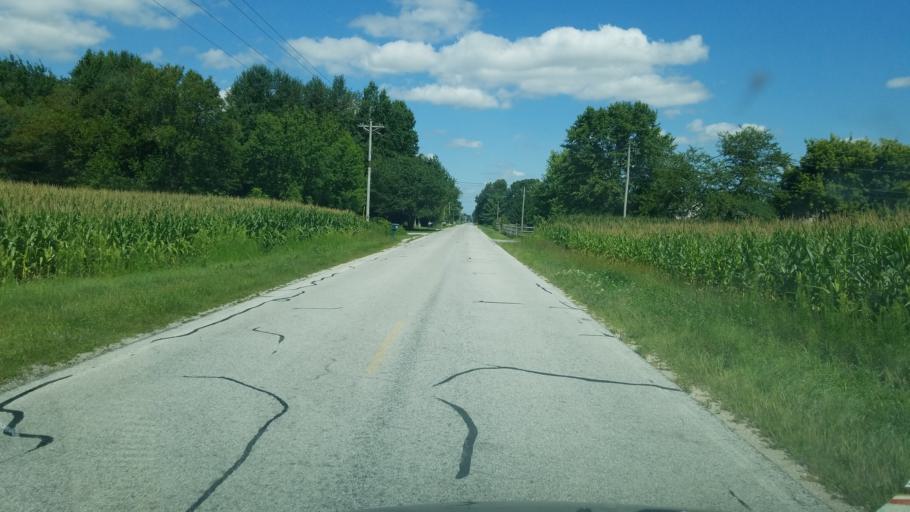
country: US
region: Ohio
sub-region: Fulton County
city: Swanton
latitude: 41.5364
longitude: -83.9409
